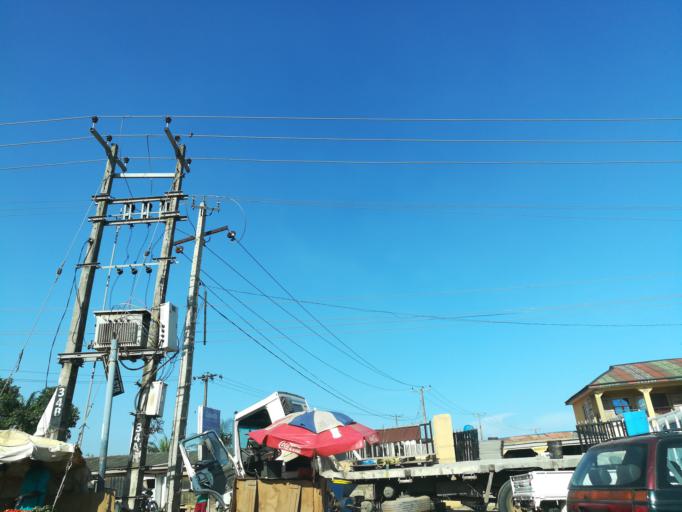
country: NG
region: Lagos
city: Ikorodu
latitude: 6.5821
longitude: 3.5250
